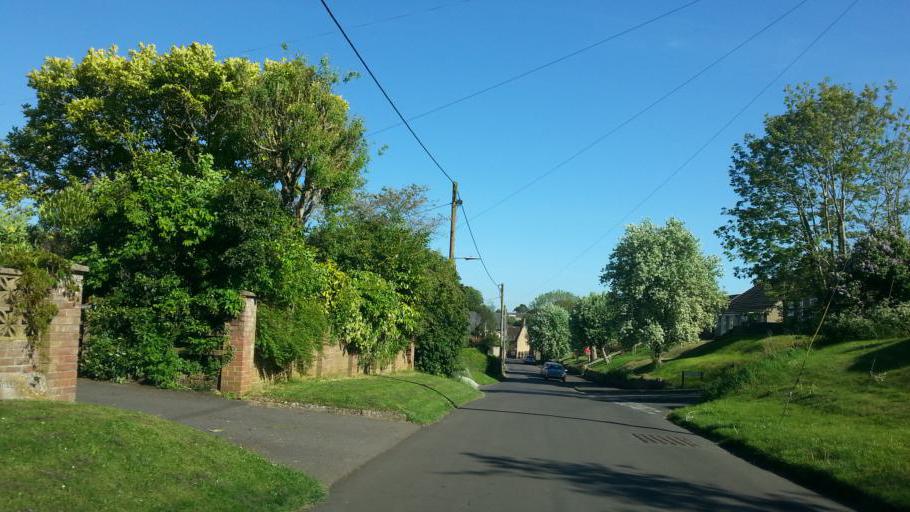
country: GB
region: England
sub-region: Somerset
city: Milborne Port
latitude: 50.9704
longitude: -2.4664
